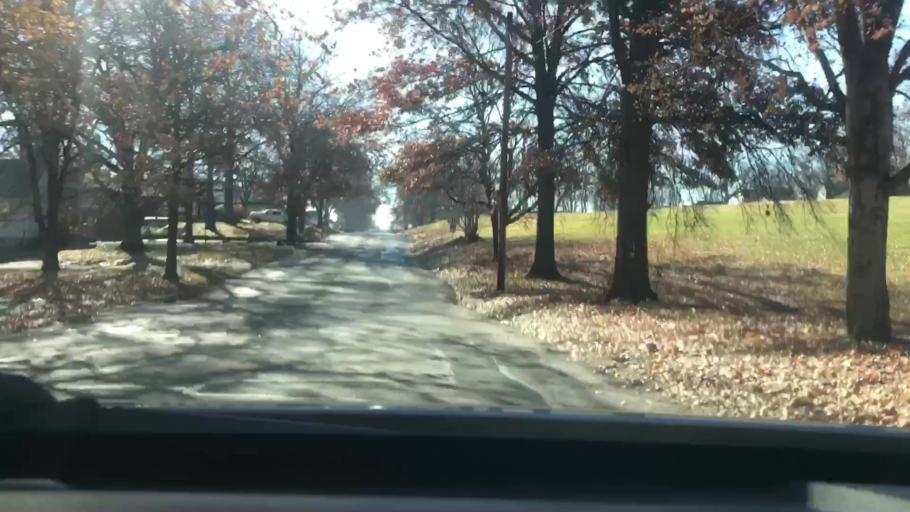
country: US
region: Kansas
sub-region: Leavenworth County
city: Leavenworth
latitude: 39.2999
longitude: -94.9209
